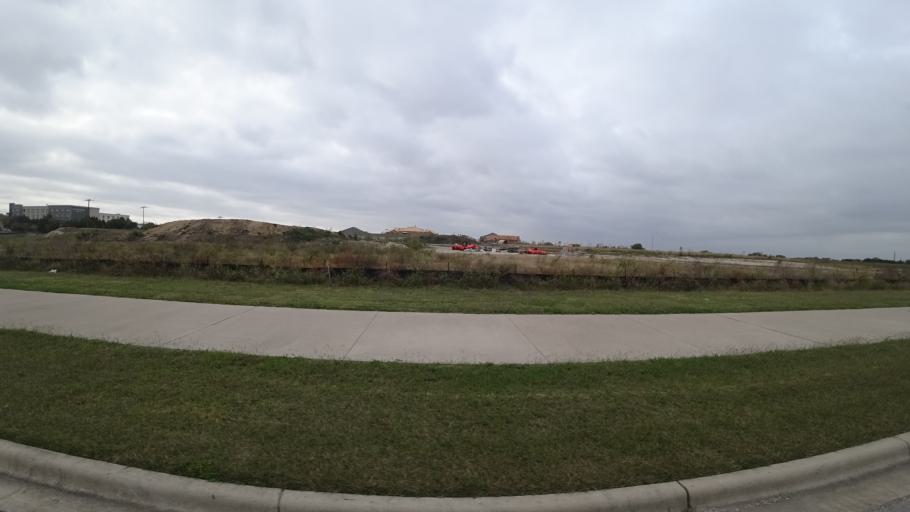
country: US
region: Texas
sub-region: Travis County
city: Pflugerville
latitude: 30.4253
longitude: -97.5923
